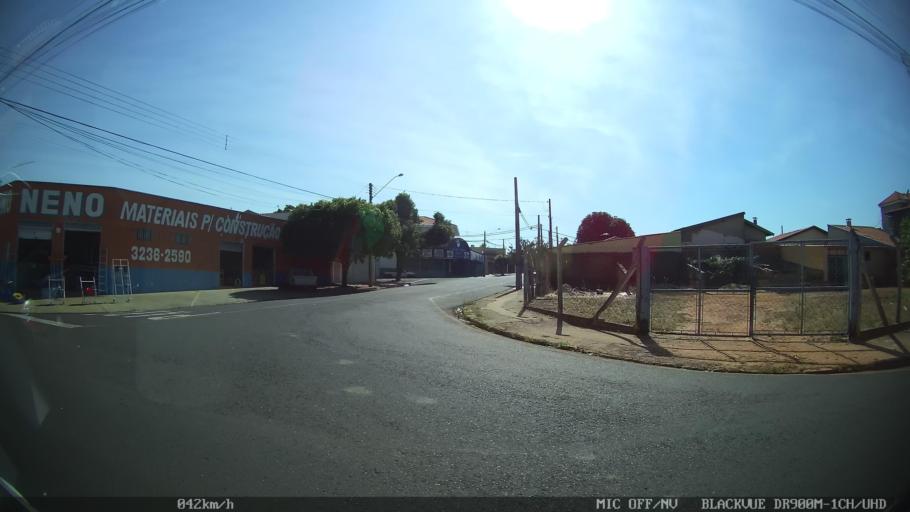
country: BR
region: Sao Paulo
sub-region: Sao Jose Do Rio Preto
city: Sao Jose do Rio Preto
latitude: -20.7872
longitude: -49.4322
